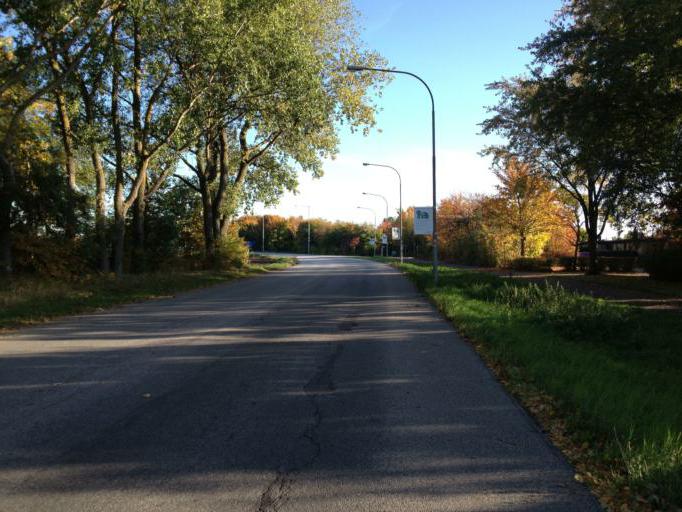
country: SE
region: Skane
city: Bjarred
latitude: 55.7275
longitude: 13.0236
